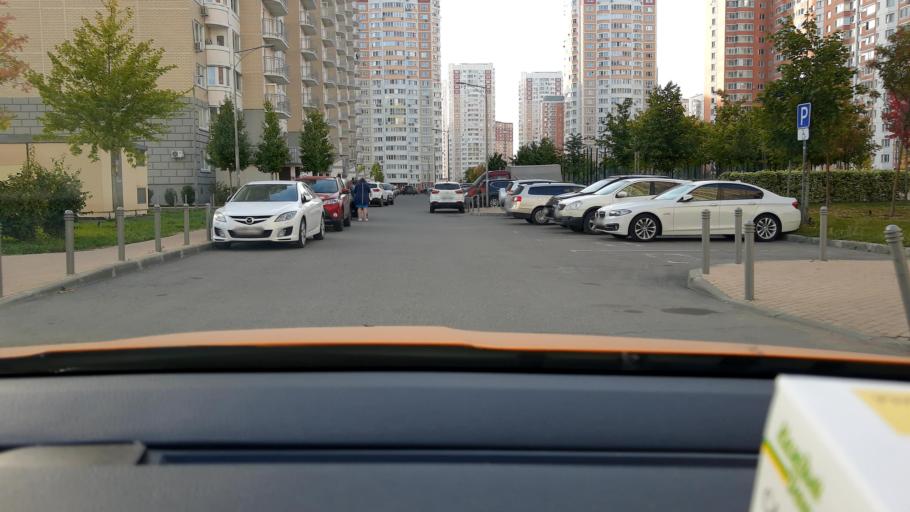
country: RU
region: Moskovskaya
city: Moskovskiy
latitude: 55.6014
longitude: 37.3653
